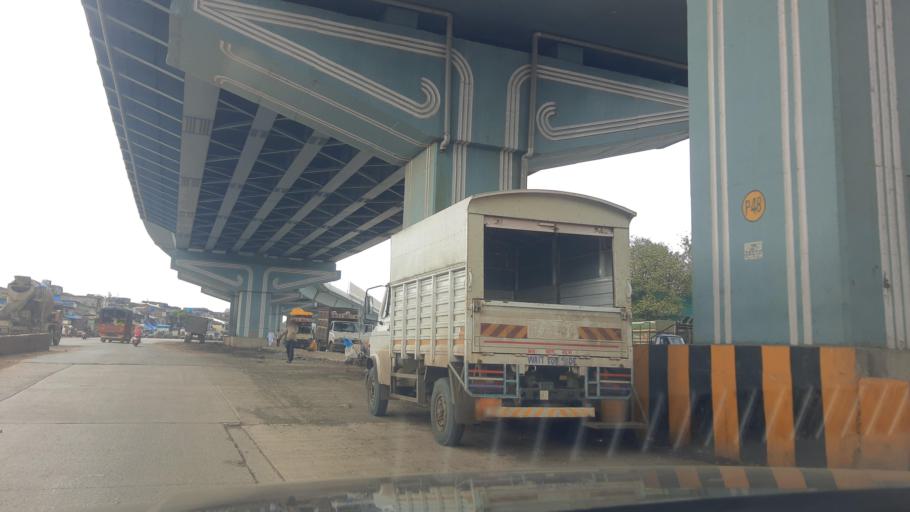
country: IN
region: Maharashtra
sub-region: Mumbai Suburban
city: Mumbai
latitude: 19.0564
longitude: 72.9301
